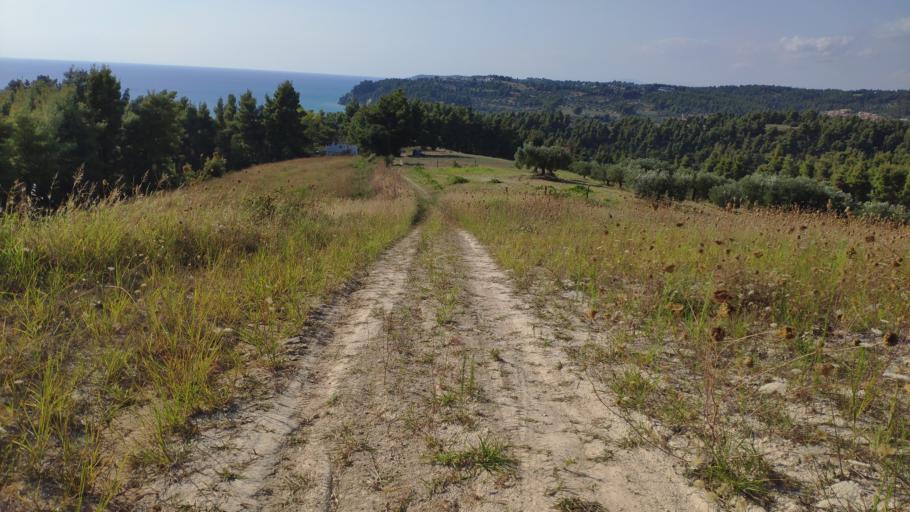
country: GR
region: Central Macedonia
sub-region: Nomos Chalkidikis
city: Kassandreia
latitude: 40.0287
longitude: 23.3690
